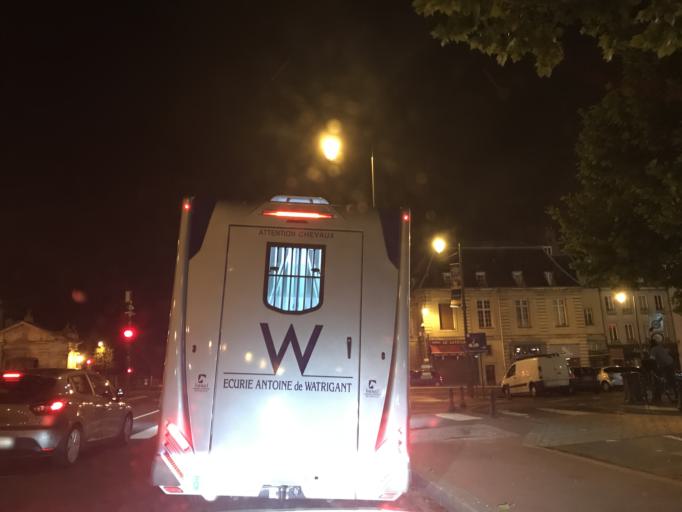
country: FR
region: Ile-de-France
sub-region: Departement des Yvelines
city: Maisons-Laffitte
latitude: 48.9475
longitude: 2.1473
